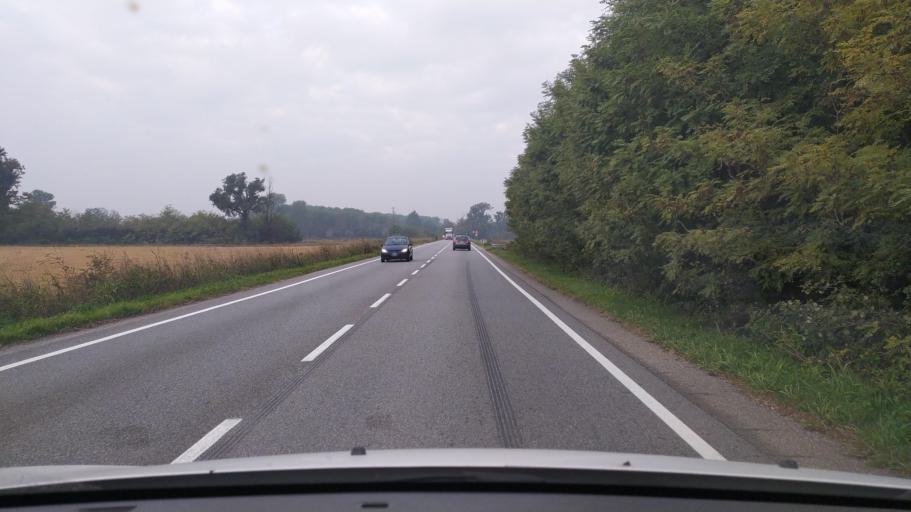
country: IT
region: Lombardy
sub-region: Citta metropolitana di Milano
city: Cisliano
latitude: 45.4446
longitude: 9.0122
